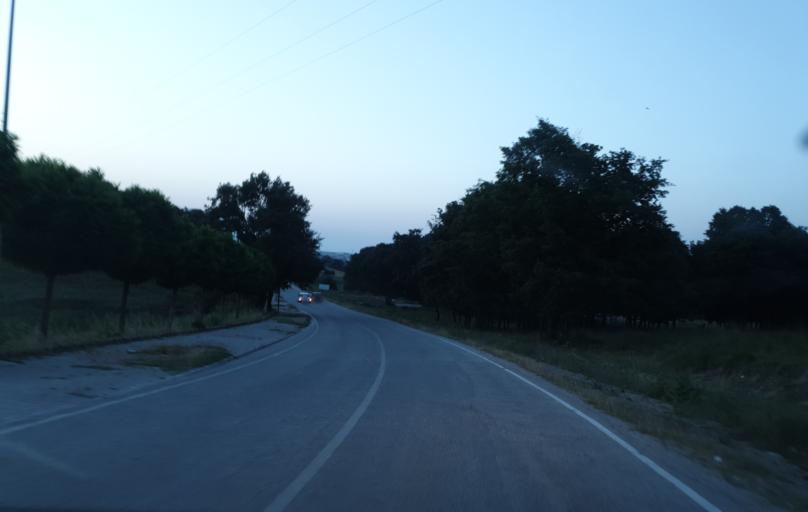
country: TR
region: Tekirdag
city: Saray
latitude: 41.3637
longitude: 27.9293
